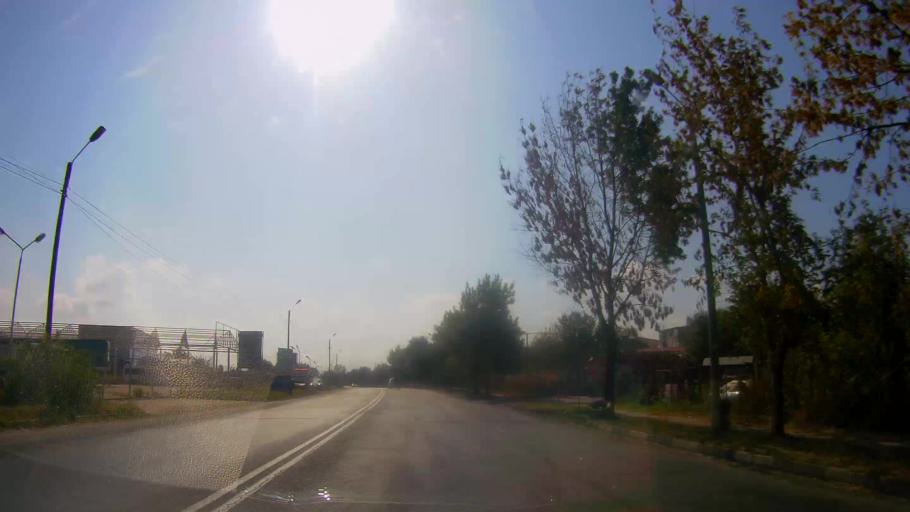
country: RO
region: Giurgiu
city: Giurgiu
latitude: 43.9123
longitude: 25.9746
